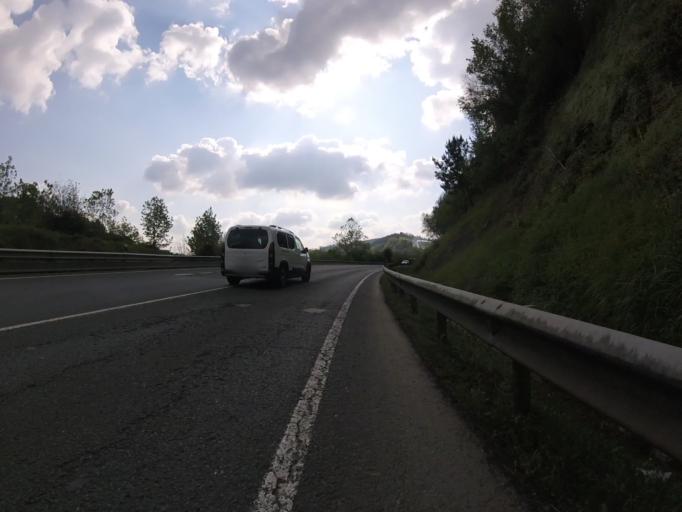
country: ES
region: Basque Country
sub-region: Provincia de Guipuzcoa
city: Azkoitia
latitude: 43.1743
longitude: -2.3149
